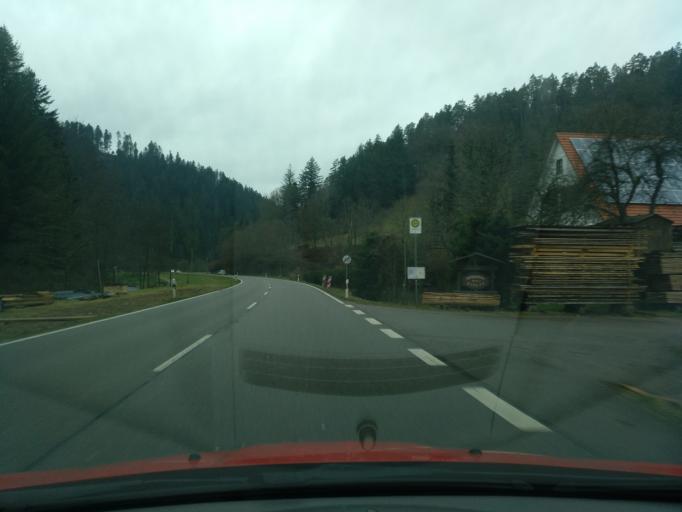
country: DE
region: Baden-Wuerttemberg
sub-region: Freiburg Region
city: Schiltach
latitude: 48.2734
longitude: 8.3577
